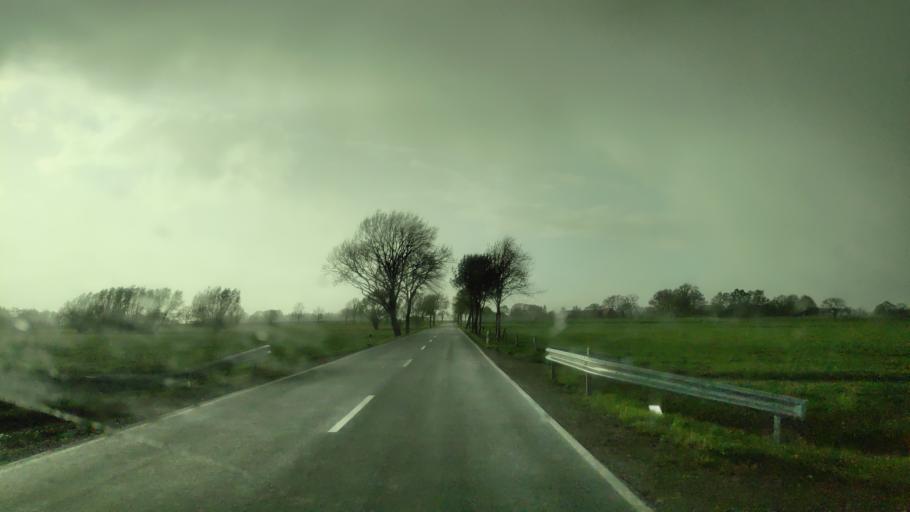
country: DE
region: North Rhine-Westphalia
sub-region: Regierungsbezirk Detmold
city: Hille
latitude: 52.3441
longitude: 8.8274
